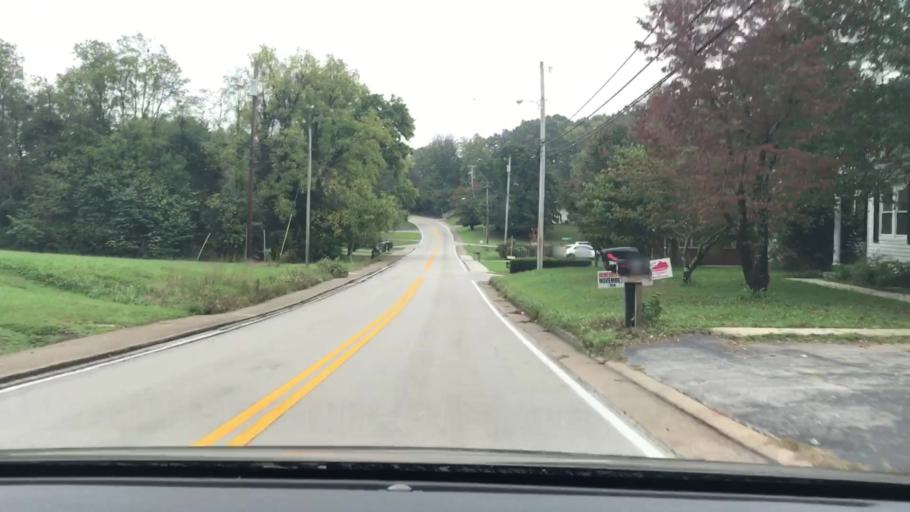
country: US
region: Kentucky
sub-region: Pulaski County
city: Somerset
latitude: 37.0926
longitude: -84.5932
